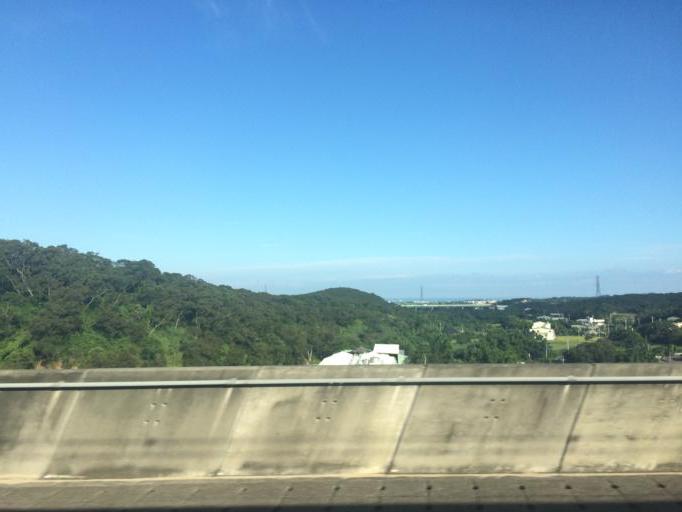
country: TW
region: Taiwan
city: Fengyuan
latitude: 24.4318
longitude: 120.6967
